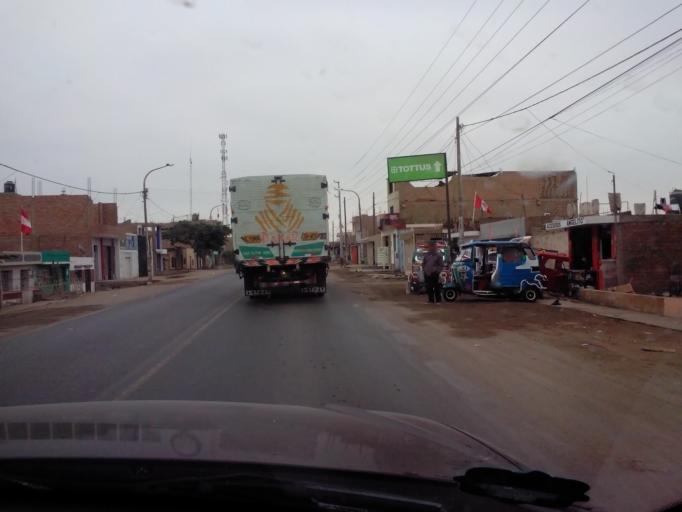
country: PE
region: Ica
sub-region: Provincia de Chincha
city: Chincha Alta
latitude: -13.4298
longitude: -76.1341
